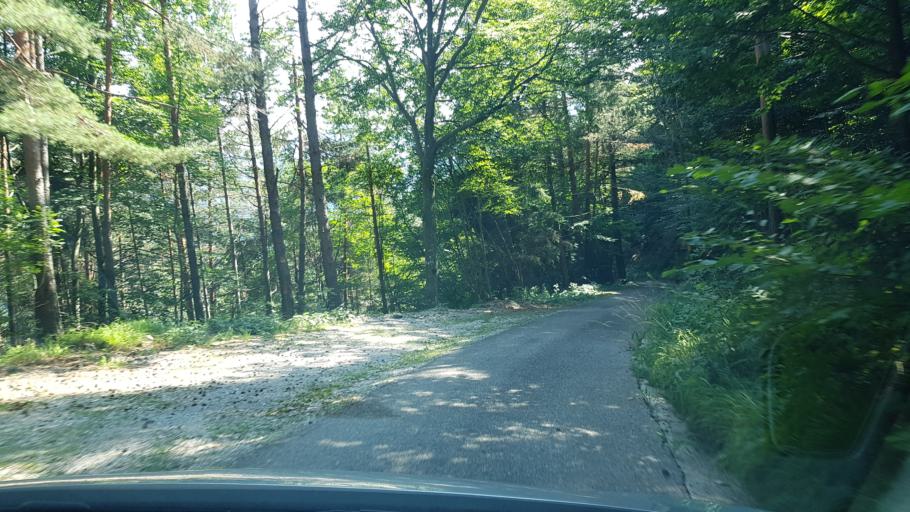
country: IT
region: Friuli Venezia Giulia
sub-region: Provincia di Udine
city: Moggio Udinese
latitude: 46.4416
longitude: 13.2121
